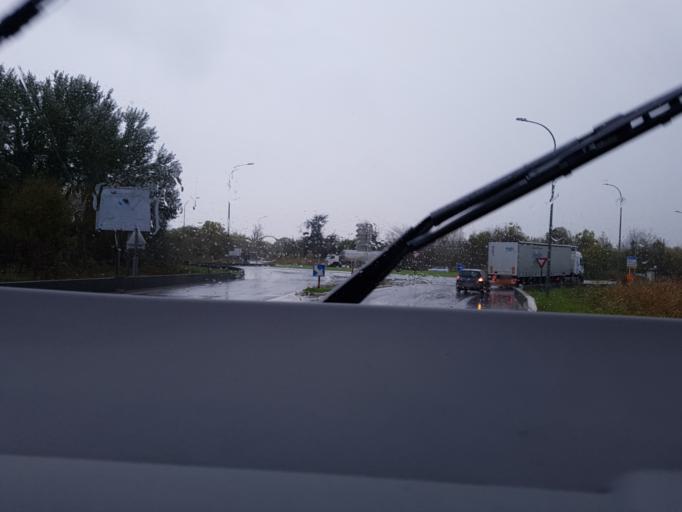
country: FR
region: Aquitaine
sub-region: Departement de la Gironde
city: Bassens
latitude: 44.9189
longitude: -0.5438
